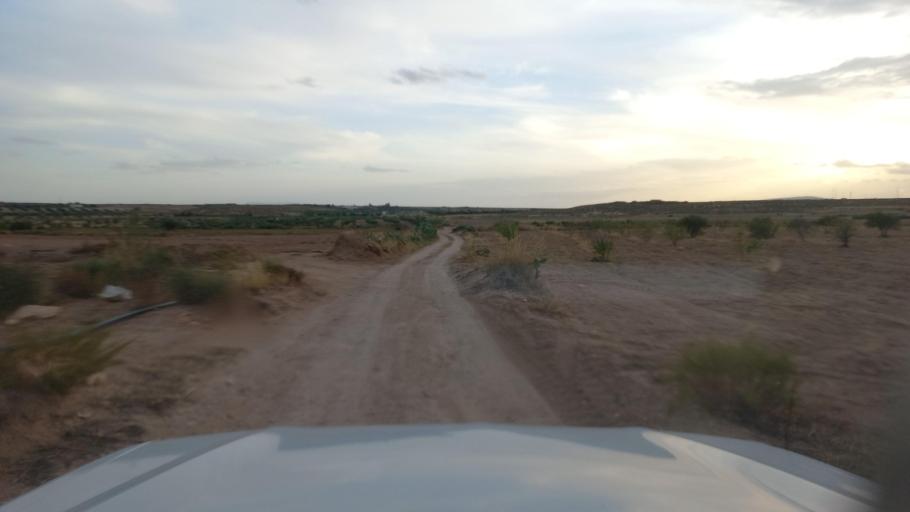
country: TN
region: Al Qasrayn
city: Sbiba
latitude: 35.4150
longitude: 9.0857
